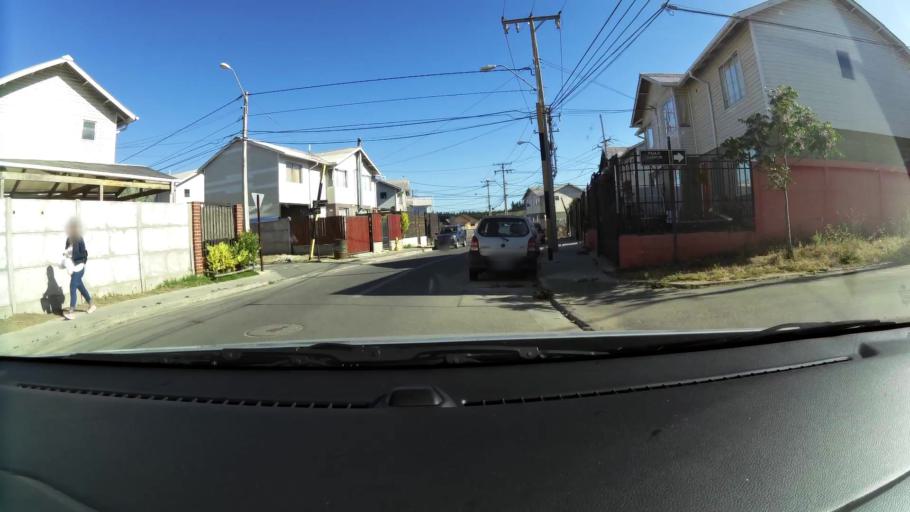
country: CL
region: Valparaiso
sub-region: Provincia de Valparaiso
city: Valparaiso
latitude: -33.1199
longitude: -71.5842
